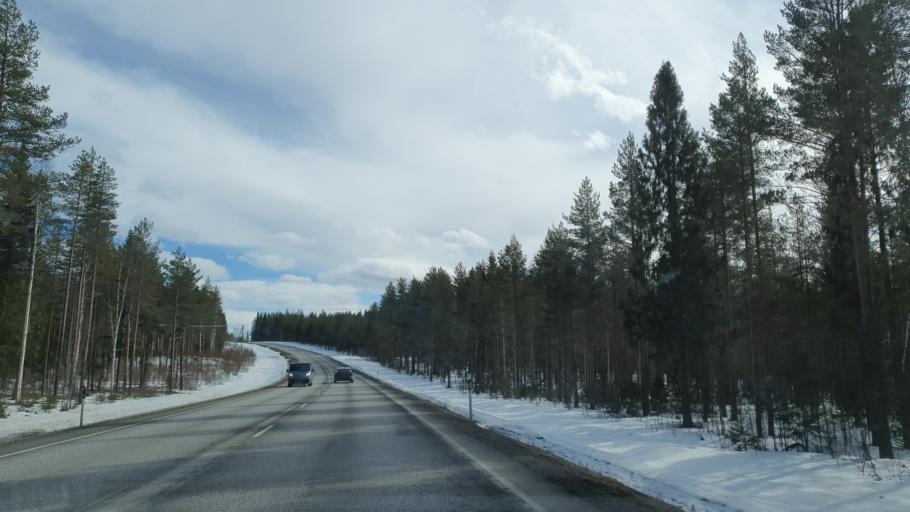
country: FI
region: Kainuu
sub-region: Kajaani
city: Paltamo
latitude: 64.3729
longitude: 28.0304
